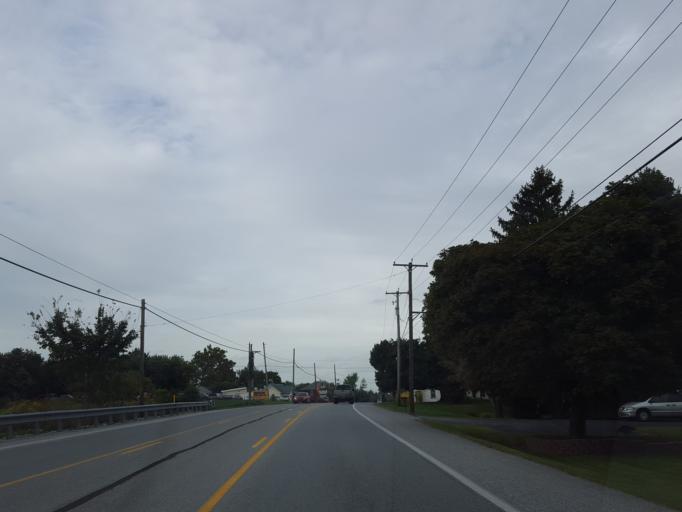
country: US
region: Pennsylvania
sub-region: Adams County
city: Abbottstown
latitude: 39.8907
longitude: -76.9685
